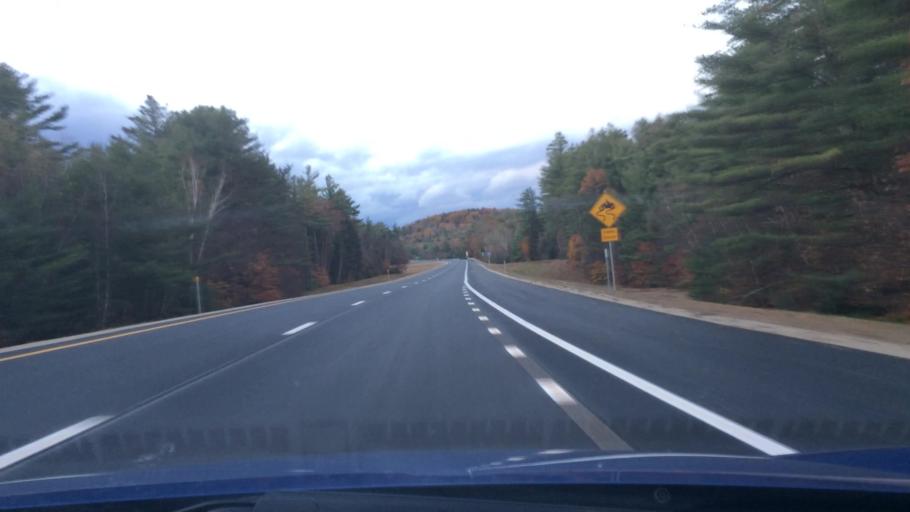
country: US
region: New Hampshire
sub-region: Grafton County
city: Thornton
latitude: 43.8751
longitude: -71.6738
